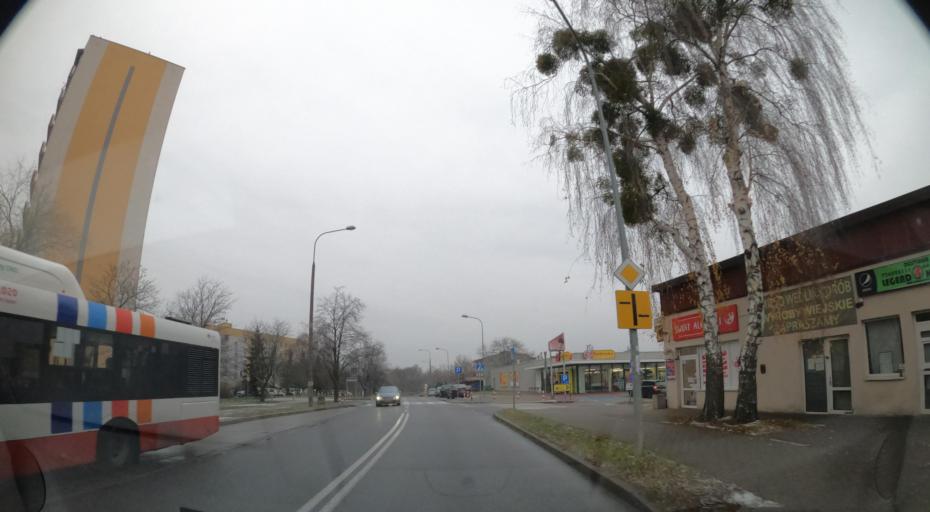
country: PL
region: Masovian Voivodeship
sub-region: Powiat radomski
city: Trablice
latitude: 51.3727
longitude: 21.1290
